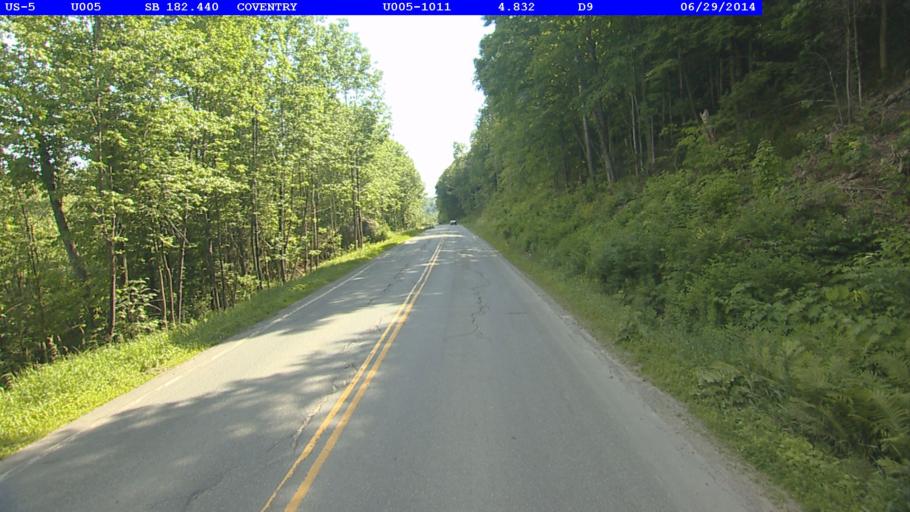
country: US
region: Vermont
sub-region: Orleans County
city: Newport
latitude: 44.9215
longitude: -72.2314
